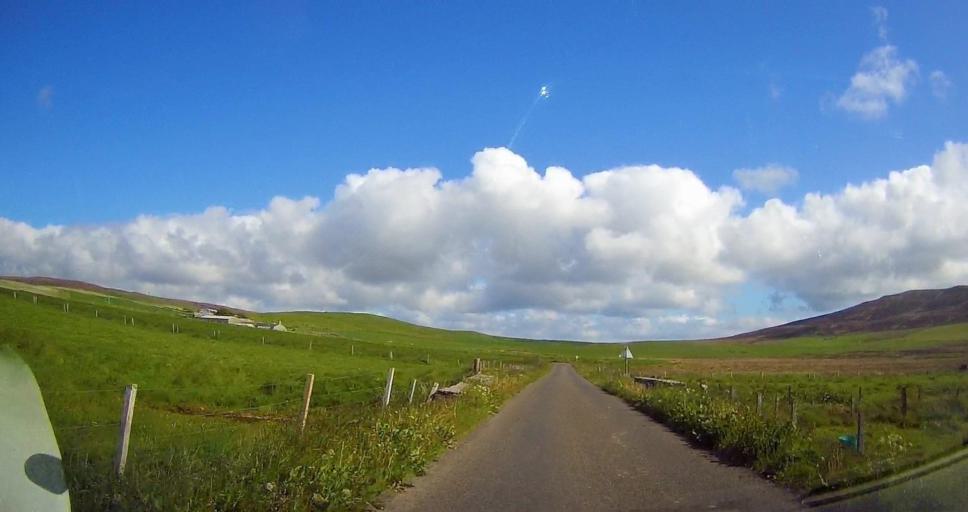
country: GB
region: Scotland
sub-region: Orkney Islands
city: Stromness
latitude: 58.9848
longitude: -3.1479
